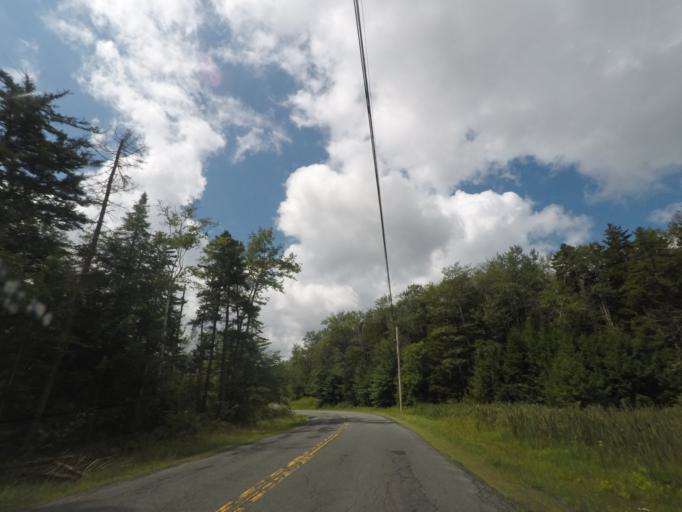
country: US
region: New York
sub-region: Rensselaer County
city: Averill Park
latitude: 42.6483
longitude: -73.4283
